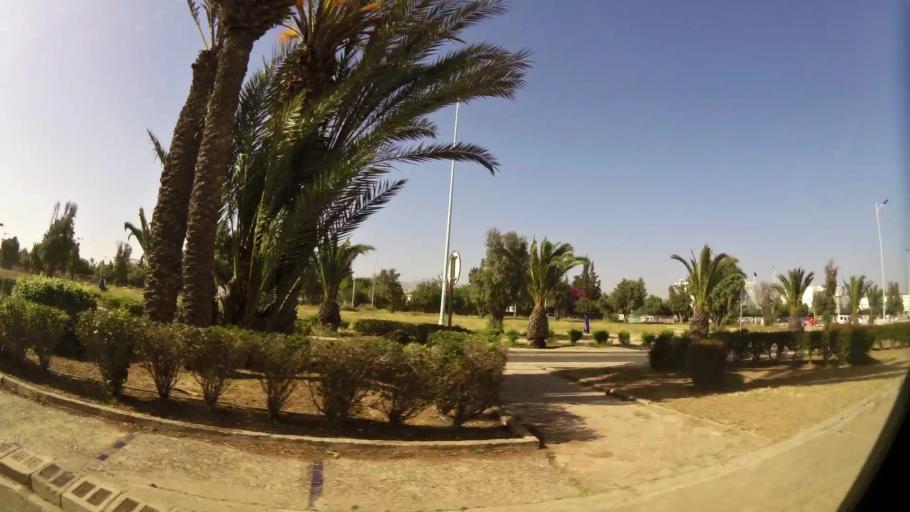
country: MA
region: Oued ed Dahab-Lagouira
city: Dakhla
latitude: 30.4043
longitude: -9.5409
